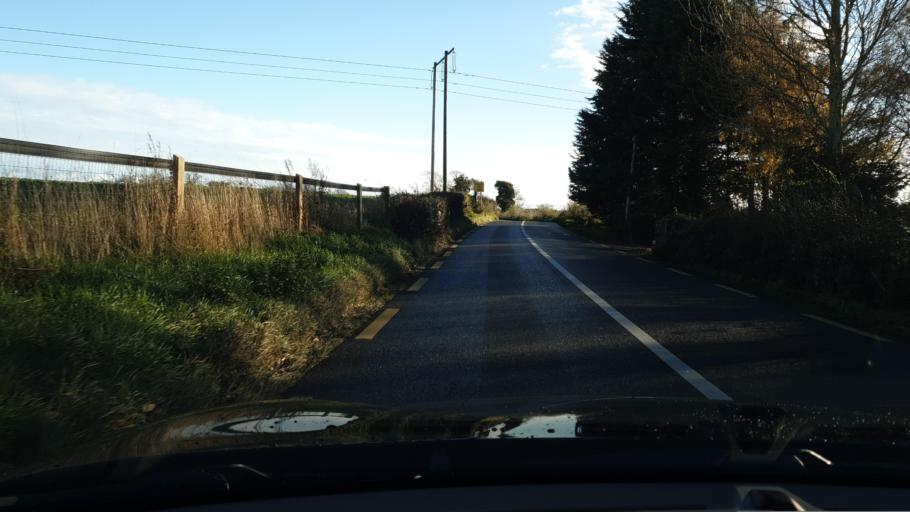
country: IE
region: Leinster
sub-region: An Mhi
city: Ashbourne
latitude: 53.4960
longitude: -6.3777
